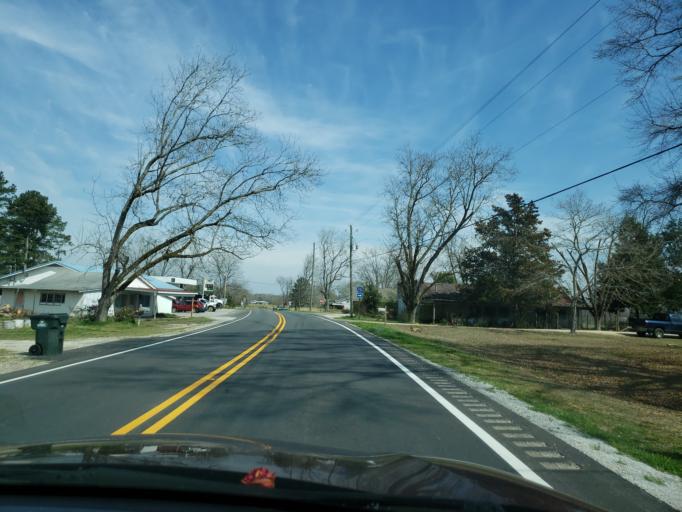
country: US
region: Alabama
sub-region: Elmore County
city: Tallassee
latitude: 32.5808
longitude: -85.7511
